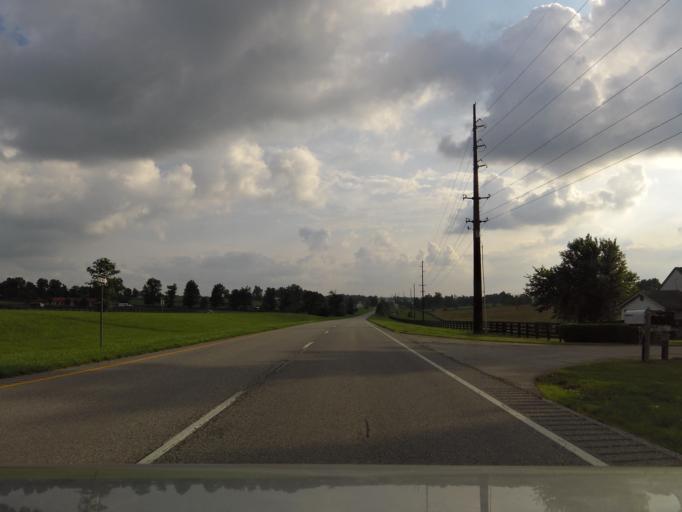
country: US
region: Kentucky
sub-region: Fayette County
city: Lexington-Fayette
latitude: 38.1277
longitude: -84.3771
